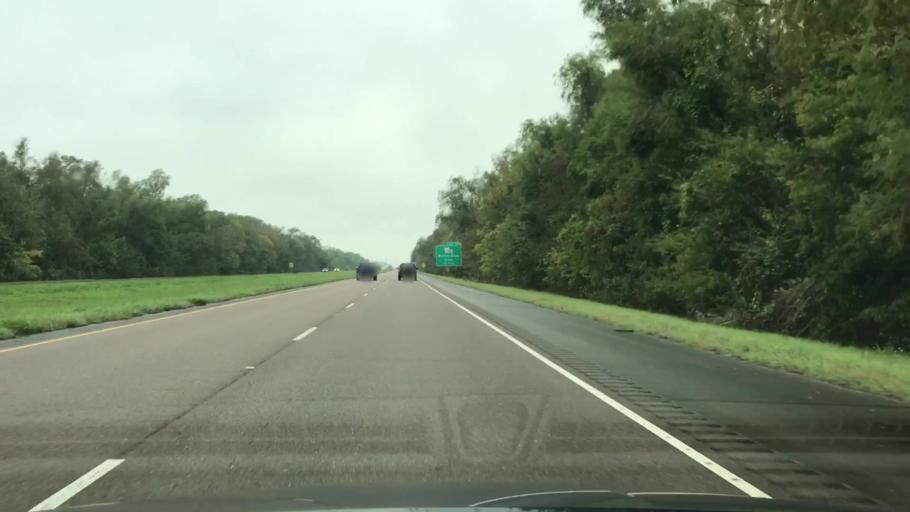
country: US
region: Louisiana
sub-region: Terrebonne Parish
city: Gray
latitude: 29.6843
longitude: -90.7342
